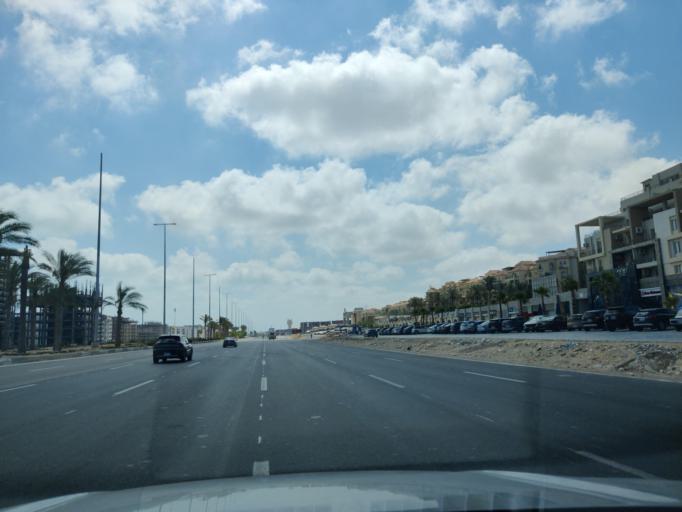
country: EG
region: Muhafazat Matruh
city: Al `Alamayn
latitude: 30.8460
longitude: 28.9310
